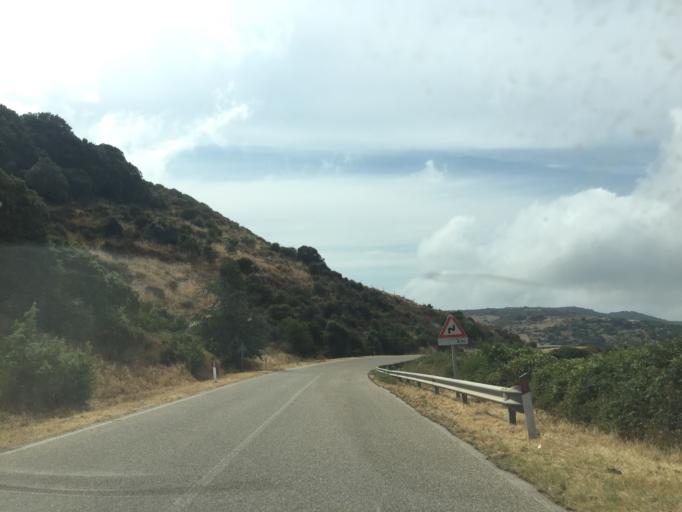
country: IT
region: Sardinia
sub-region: Provincia di Olbia-Tempio
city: Trinita d'Agultu
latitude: 40.9751
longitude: 8.9476
